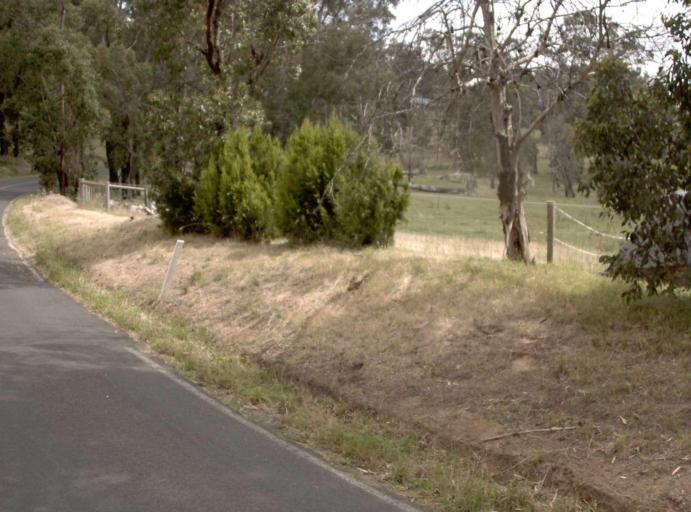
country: AU
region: Victoria
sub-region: Latrobe
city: Traralgon
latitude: -38.3173
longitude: 146.5735
